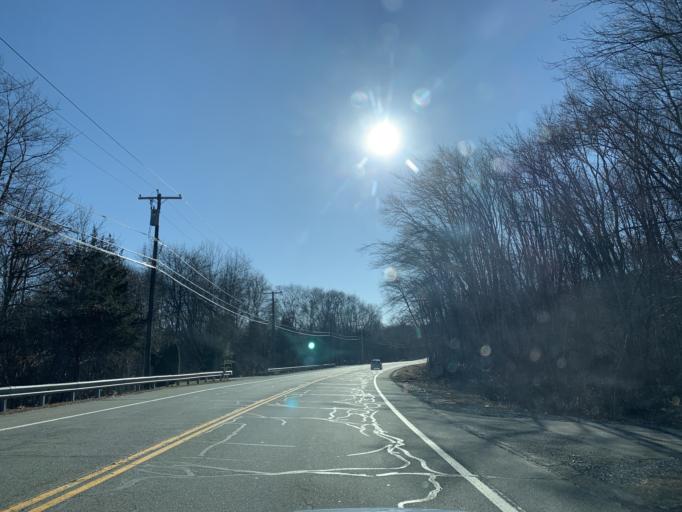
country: US
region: Rhode Island
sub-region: Providence County
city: North Providence
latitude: 41.8833
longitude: -71.4617
